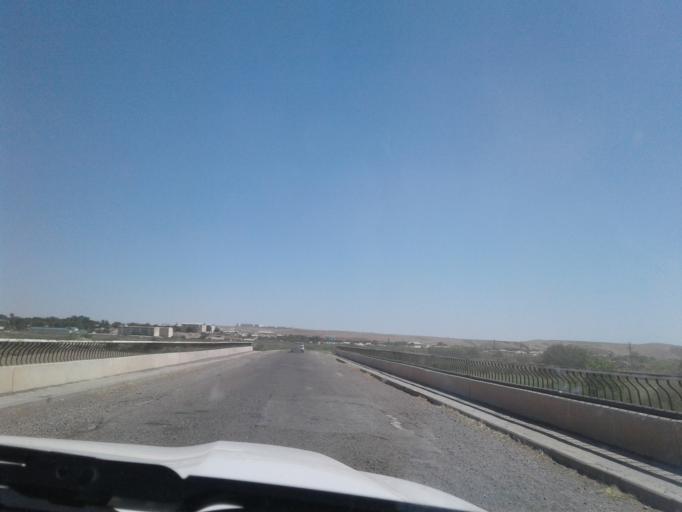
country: AF
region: Badghis
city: Bala Murghab
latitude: 35.9658
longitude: 62.9079
